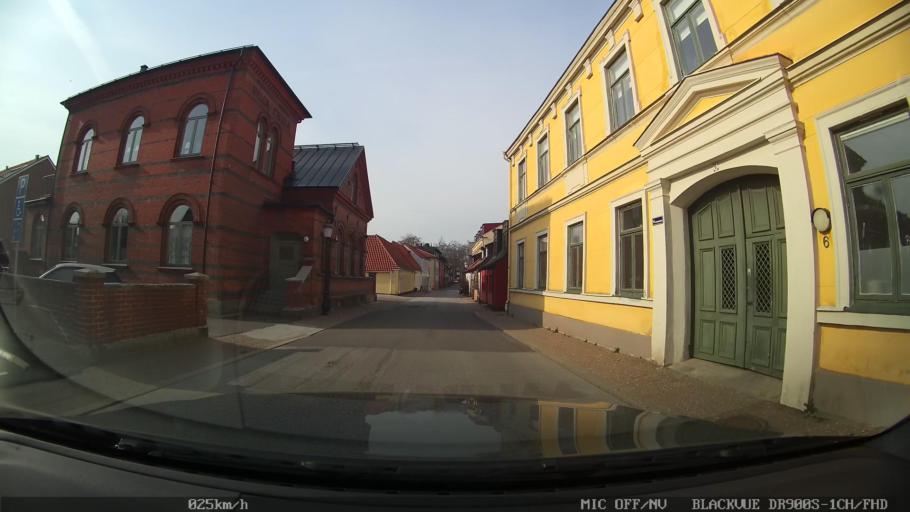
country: SE
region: Skane
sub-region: Ystads Kommun
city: Ystad
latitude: 55.4298
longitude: 13.8175
